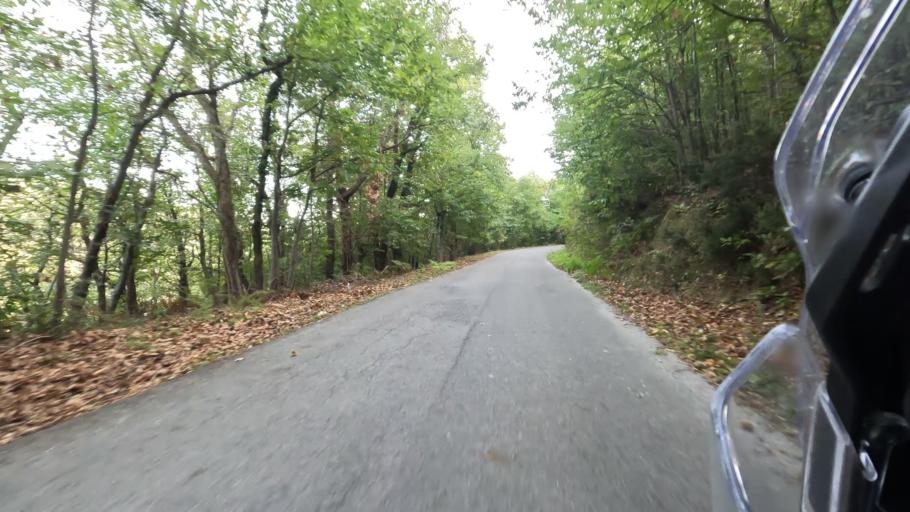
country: IT
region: Liguria
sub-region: Provincia di Savona
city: San Giovanni
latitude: 44.3937
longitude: 8.5370
